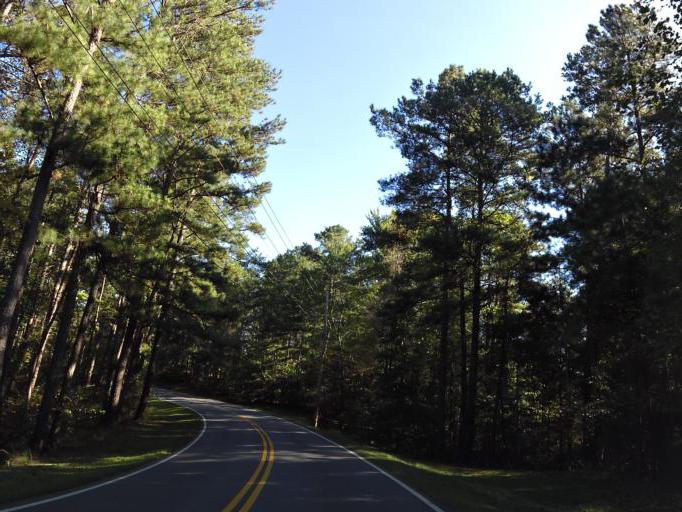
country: US
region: Georgia
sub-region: Bartow County
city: Emerson
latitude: 34.1387
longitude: -84.6986
